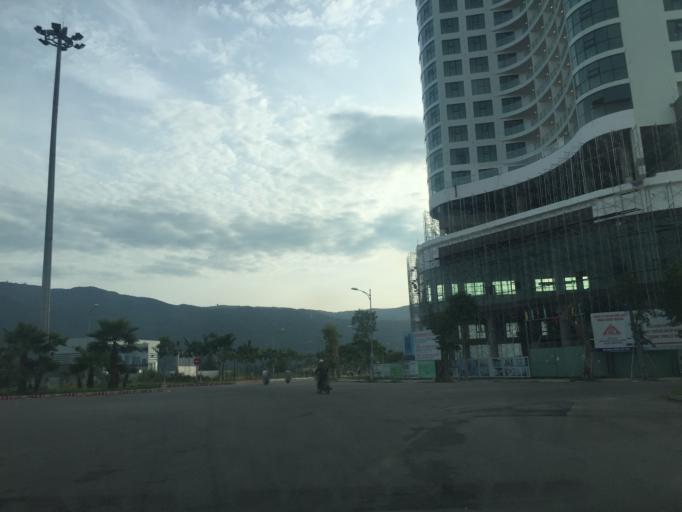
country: VN
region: Da Nang
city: Da Nang
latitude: 16.1004
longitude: 108.2315
